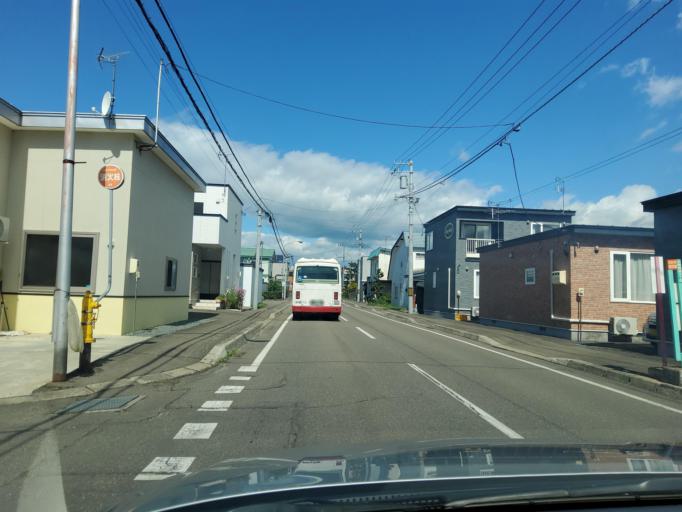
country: JP
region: Hokkaido
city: Obihiro
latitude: 42.9531
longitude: 143.2024
